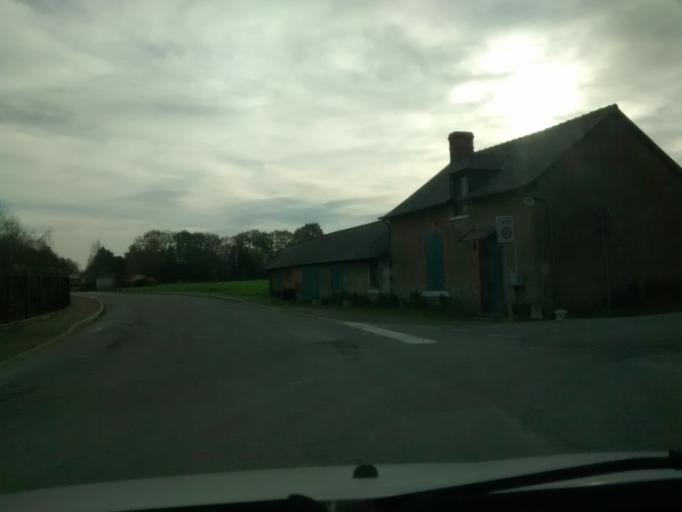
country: FR
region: Brittany
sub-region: Departement d'Ille-et-Vilaine
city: Noyal-sur-Vilaine
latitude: 48.0867
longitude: -1.5524
